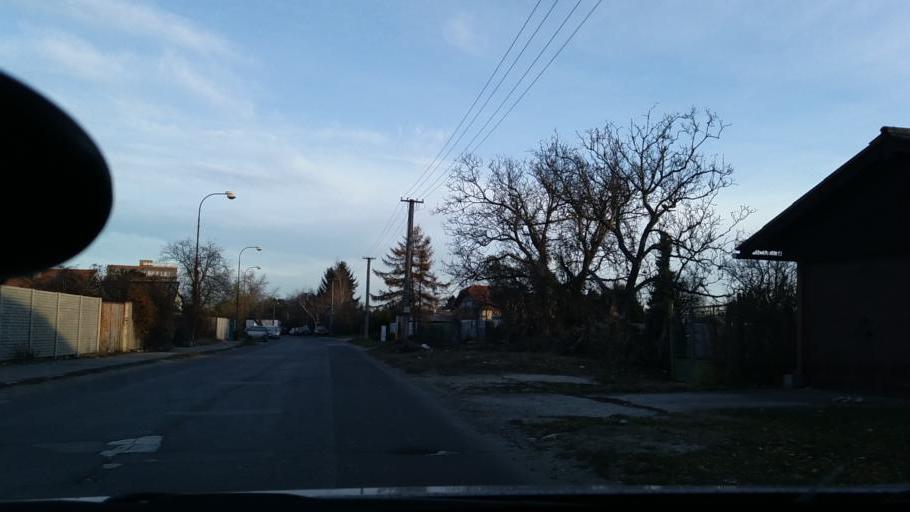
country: SK
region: Bratislavsky
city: Bratislava
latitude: 48.1326
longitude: 17.1888
